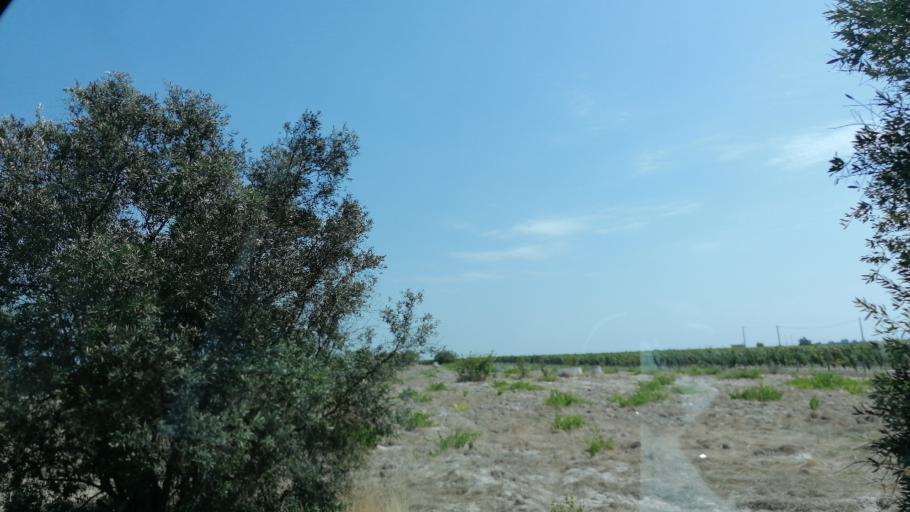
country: PT
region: Setubal
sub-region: Palmela
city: Palmela
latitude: 38.6060
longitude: -8.8413
